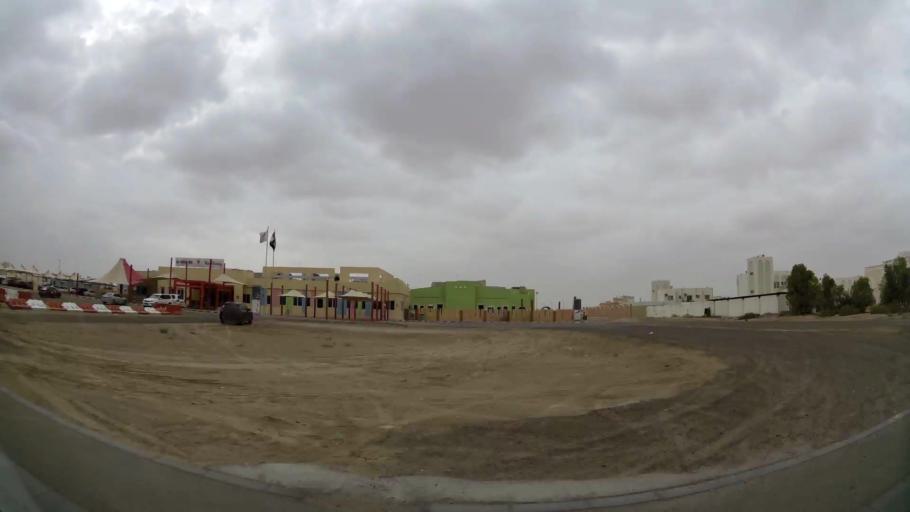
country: AE
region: Abu Dhabi
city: Abu Dhabi
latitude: 24.3291
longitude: 54.6441
